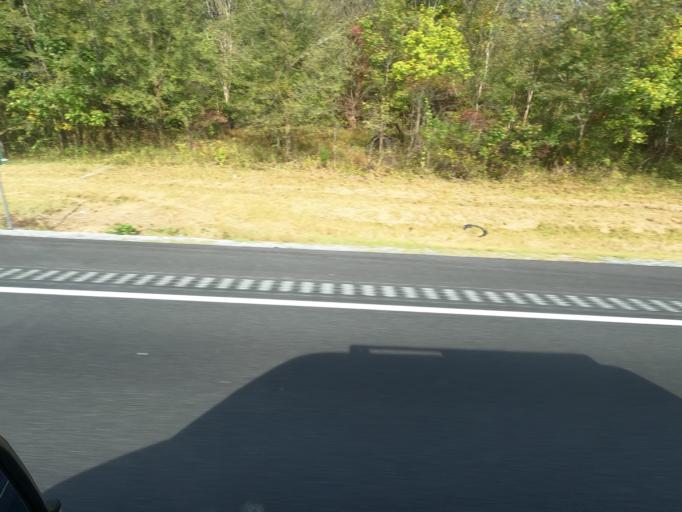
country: US
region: Tennessee
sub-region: Humphreys County
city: McEwen
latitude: 35.9271
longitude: -87.5892
